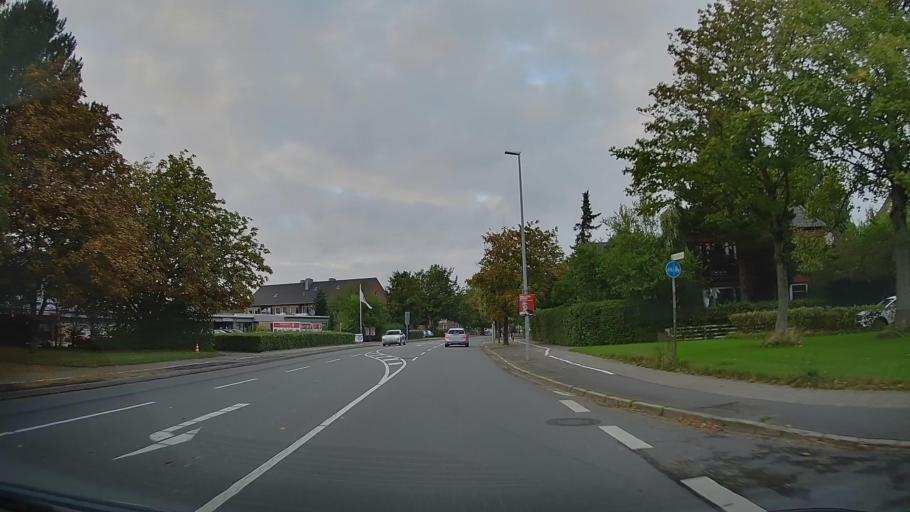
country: DE
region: Schleswig-Holstein
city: Husum
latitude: 54.4833
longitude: 9.0546
